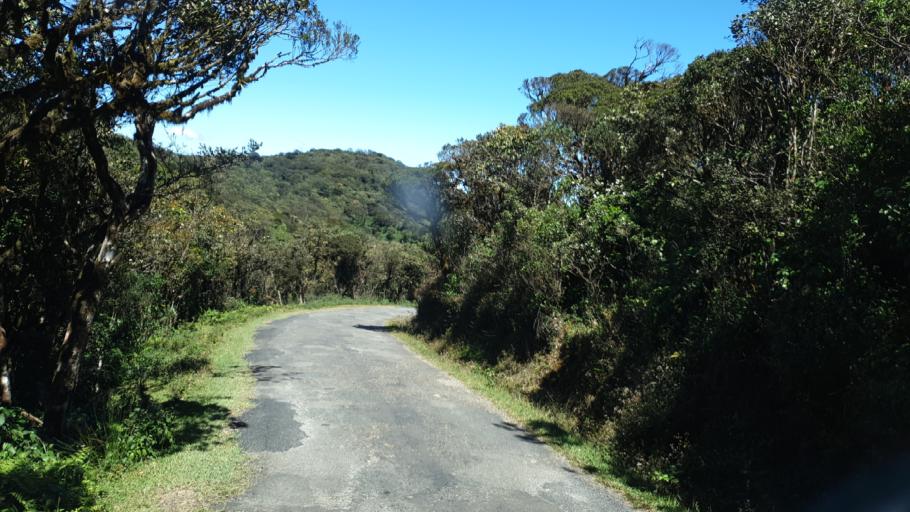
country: LK
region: Central
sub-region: Nuwara Eliya District
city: Nuwara Eliya
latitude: 6.8364
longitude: 80.8107
